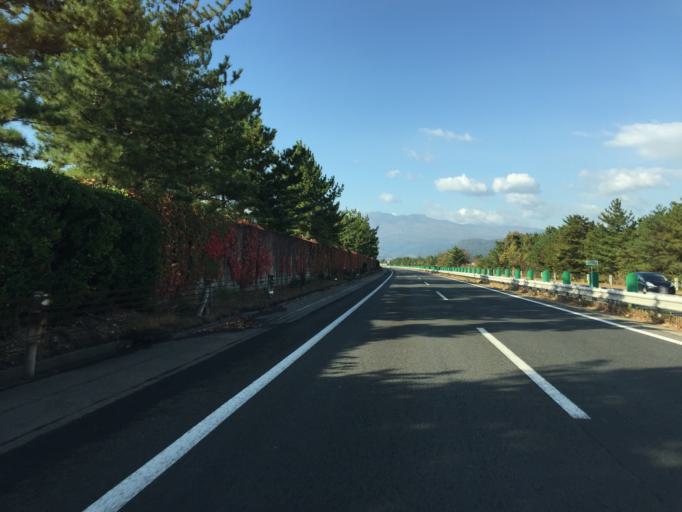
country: JP
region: Fukushima
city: Fukushima-shi
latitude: 37.7997
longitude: 140.4382
